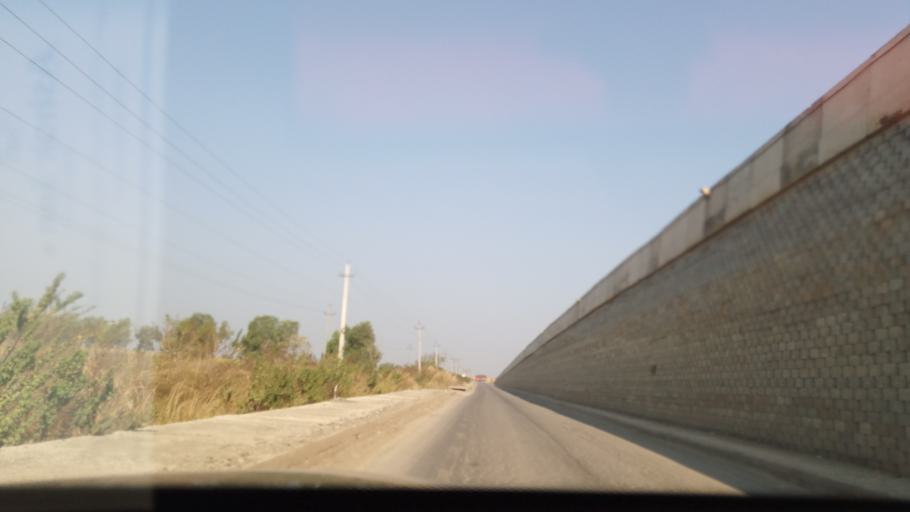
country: IN
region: Karnataka
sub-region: Haveri
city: Savanur
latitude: 14.8835
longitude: 75.3066
